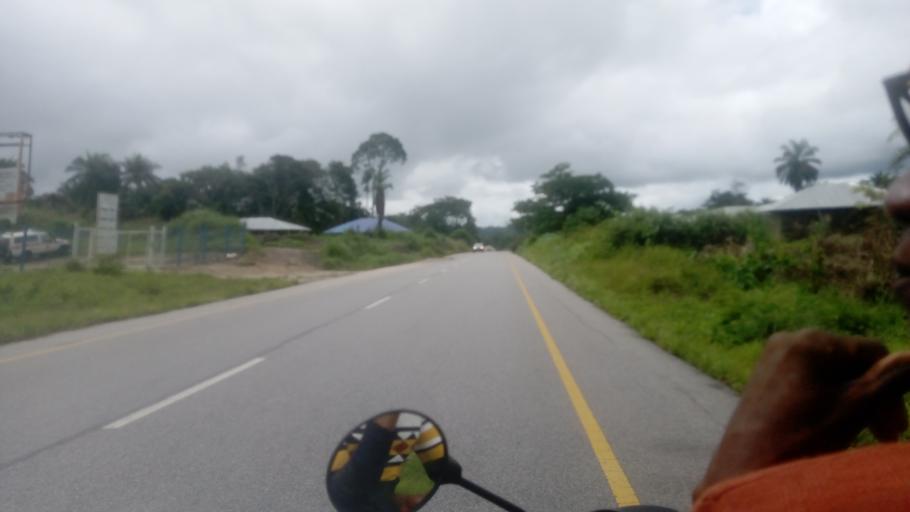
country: SL
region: Northern Province
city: Makali
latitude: 8.6323
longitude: -11.6680
